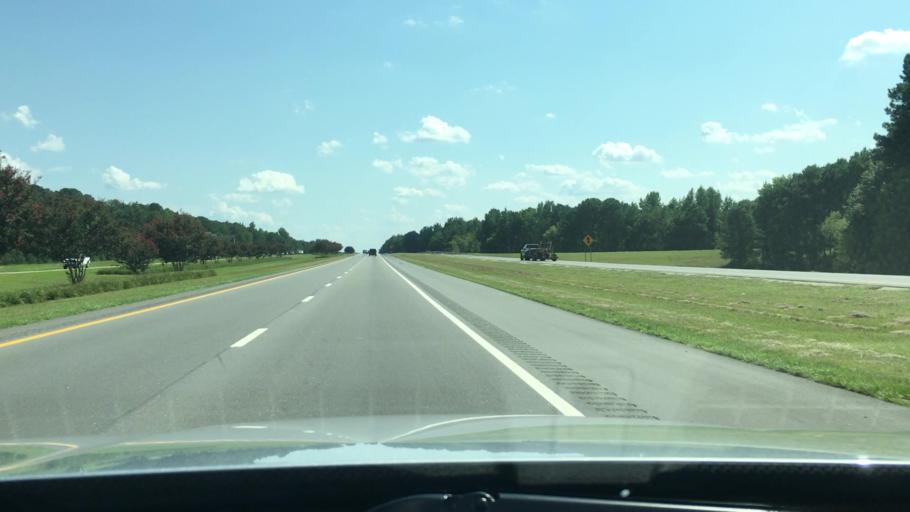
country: US
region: North Carolina
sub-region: Cumberland County
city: Vander
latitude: 35.0414
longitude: -78.8041
